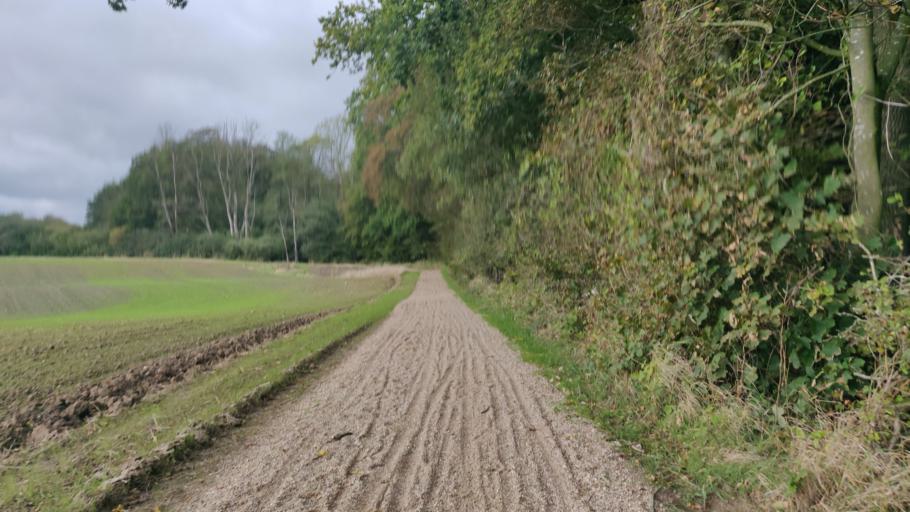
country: DK
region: South Denmark
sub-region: Kolding Kommune
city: Lunderskov
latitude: 55.5389
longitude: 9.3571
